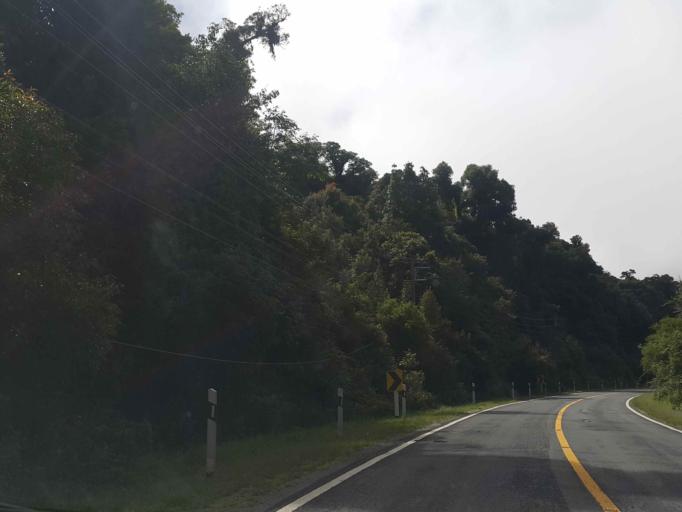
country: TH
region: Chiang Mai
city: Mae Chaem
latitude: 18.5809
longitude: 98.4804
